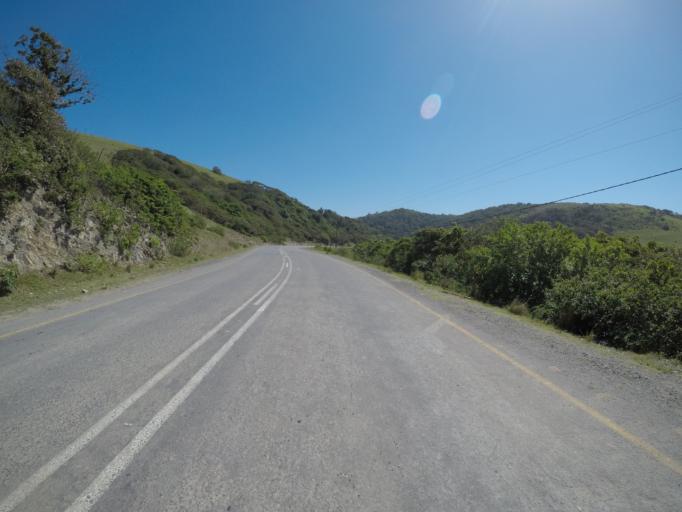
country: ZA
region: Eastern Cape
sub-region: OR Tambo District Municipality
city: Libode
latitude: -31.9811
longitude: 29.1478
